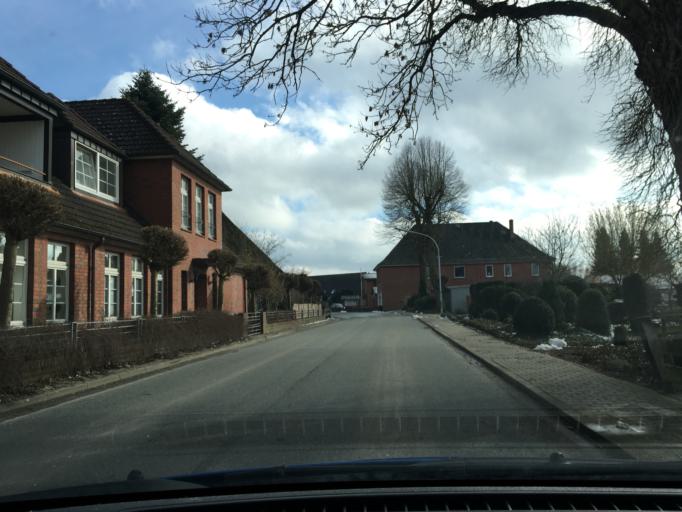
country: DE
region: Lower Saxony
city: Handorf
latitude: 53.3475
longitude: 10.3429
